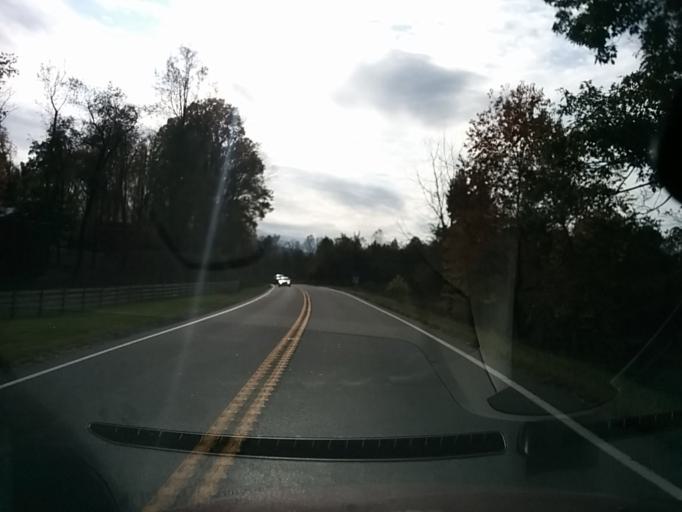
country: US
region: Virginia
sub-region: Nelson County
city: Nellysford
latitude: 37.8820
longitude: -78.9054
